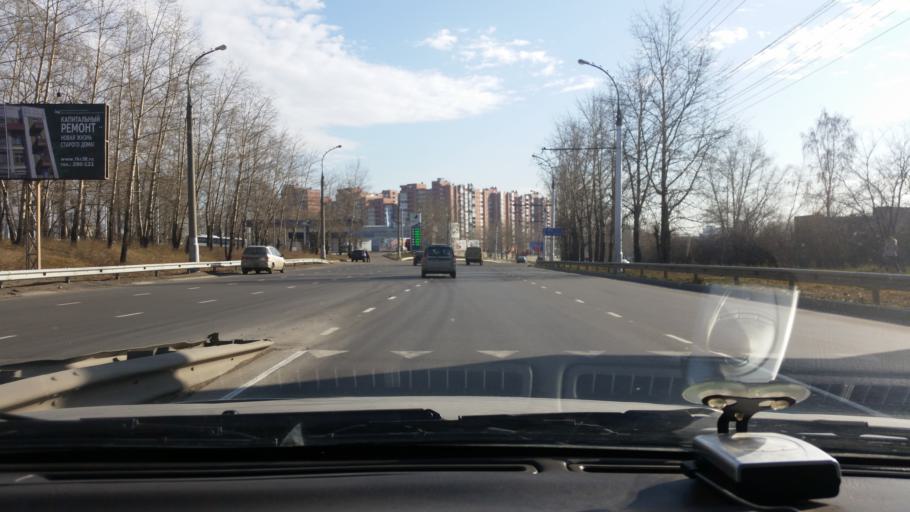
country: RU
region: Irkutsk
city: Dzerzhinsk
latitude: 52.2637
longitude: 104.3492
